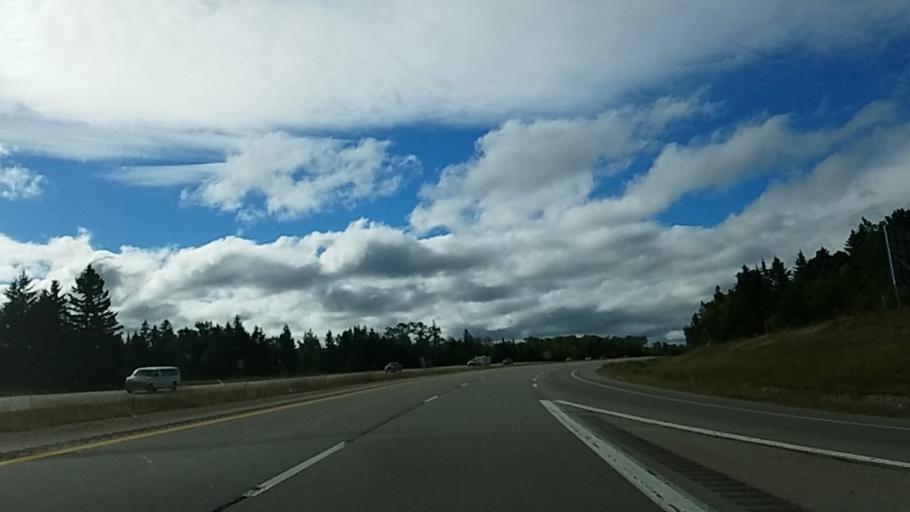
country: US
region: Michigan
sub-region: Mackinac County
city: Saint Ignace
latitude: 45.7605
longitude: -84.7298
